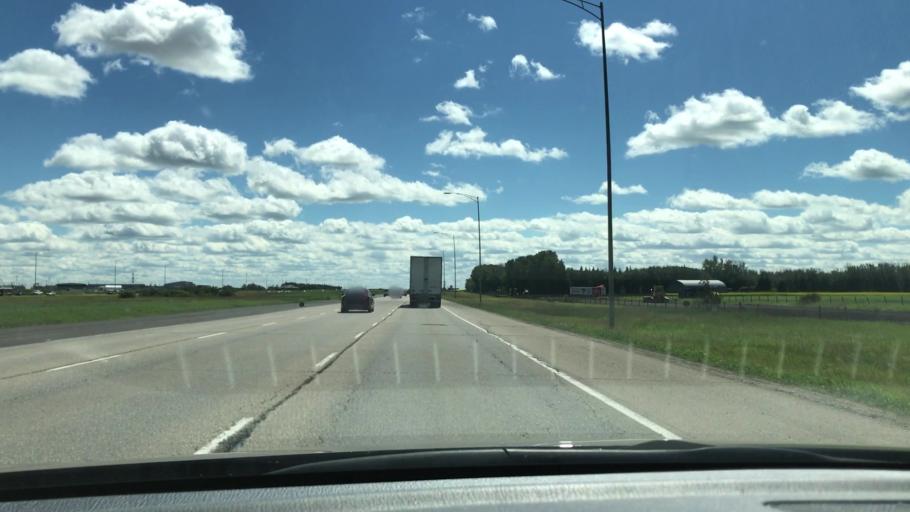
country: CA
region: Alberta
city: Leduc
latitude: 53.3662
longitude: -113.5323
